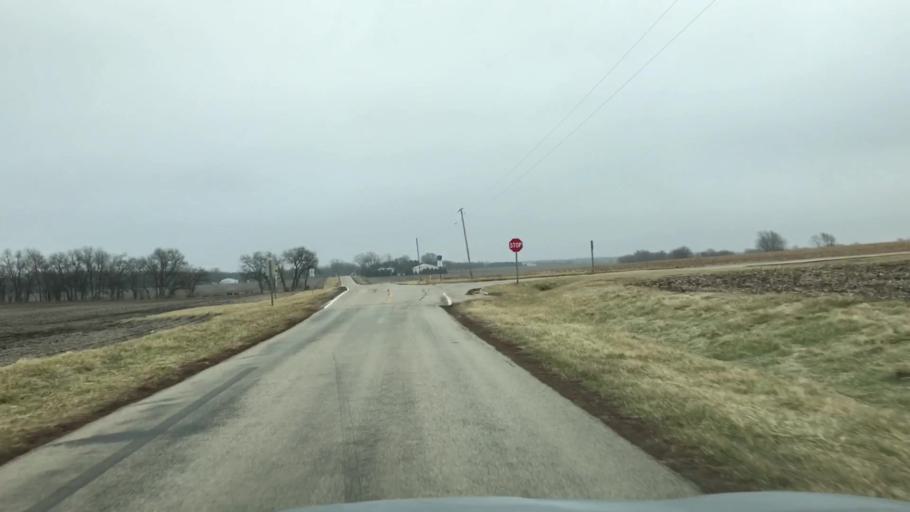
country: US
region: Illinois
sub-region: McLean County
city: Hudson
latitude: 40.6275
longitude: -88.9464
